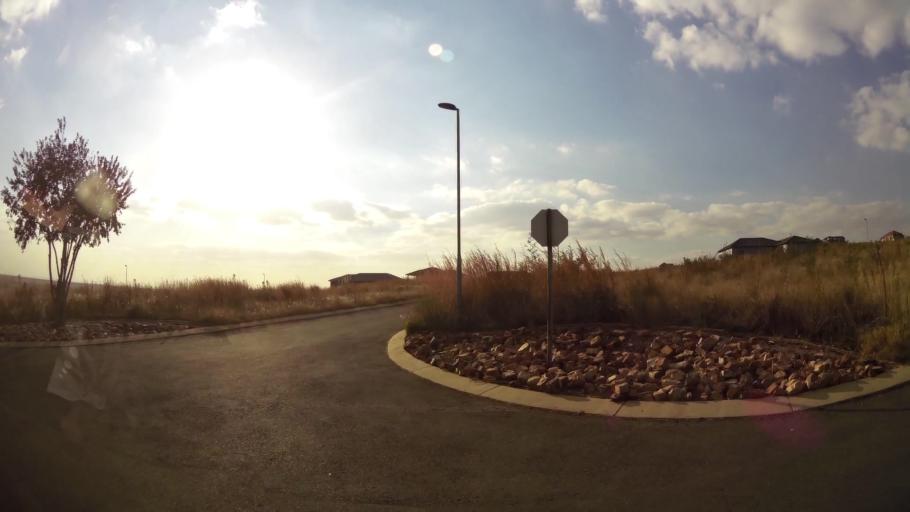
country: ZA
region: Gauteng
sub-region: West Rand District Municipality
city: Krugersdorp
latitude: -26.1046
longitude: 27.7302
